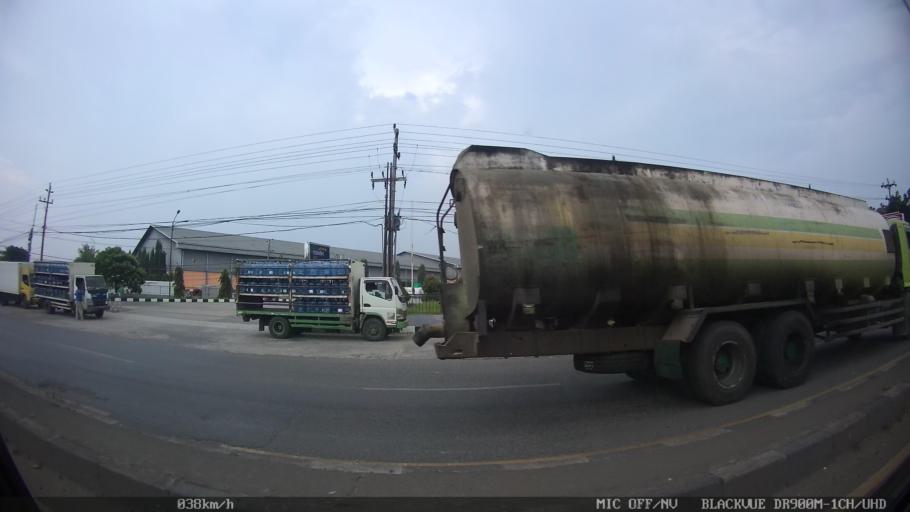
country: ID
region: Lampung
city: Bandarlampung
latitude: -5.4106
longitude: 105.2945
